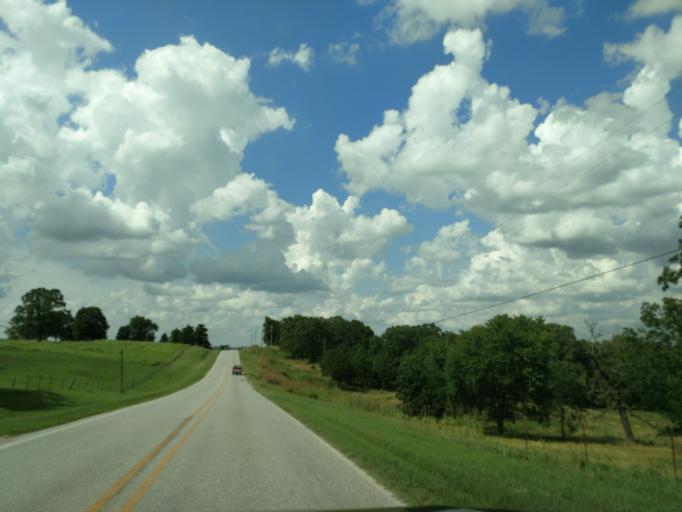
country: US
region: Arkansas
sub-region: Carroll County
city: Berryville
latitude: 36.4462
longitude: -93.5561
